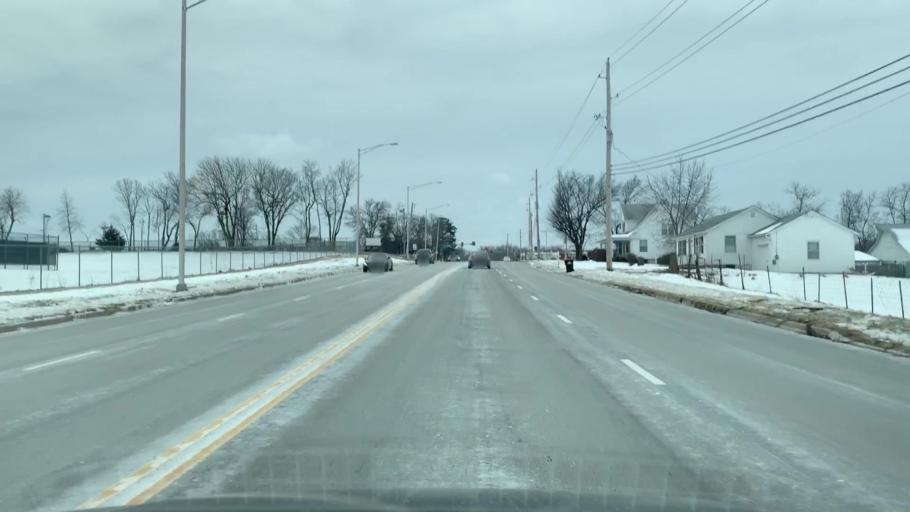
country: US
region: Missouri
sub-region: Jackson County
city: Lees Summit
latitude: 38.9274
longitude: -94.3797
